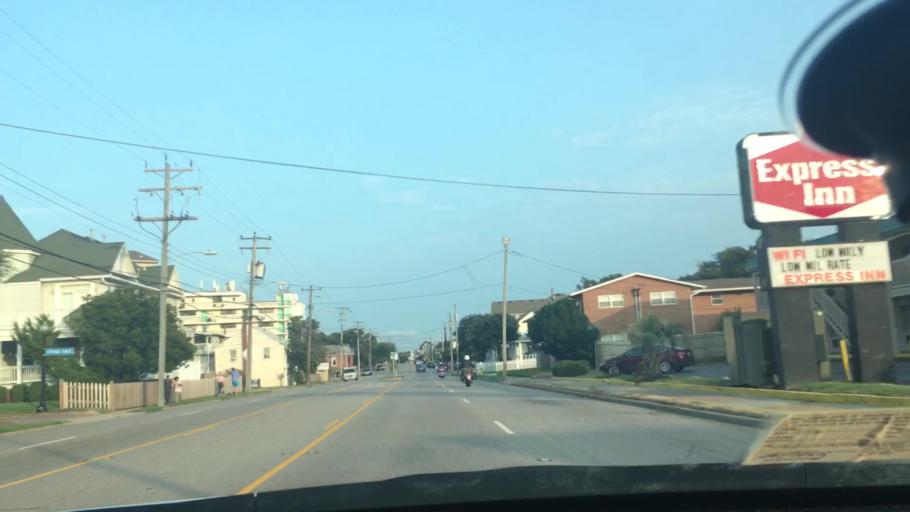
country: US
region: Virginia
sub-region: City of Norfolk
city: Norfolk
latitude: 36.9457
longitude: -76.2383
